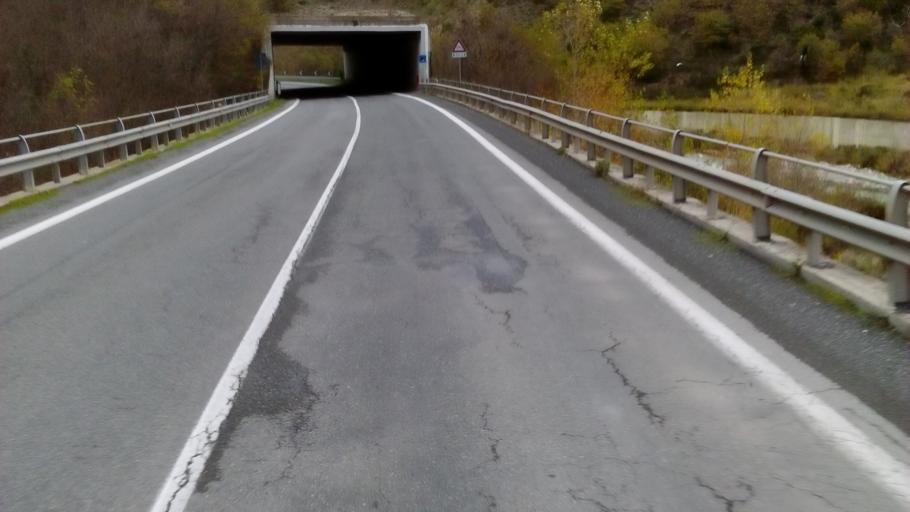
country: IT
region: Molise
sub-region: Provincia di Campobasso
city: Trivento
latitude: 41.7905
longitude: 14.5354
